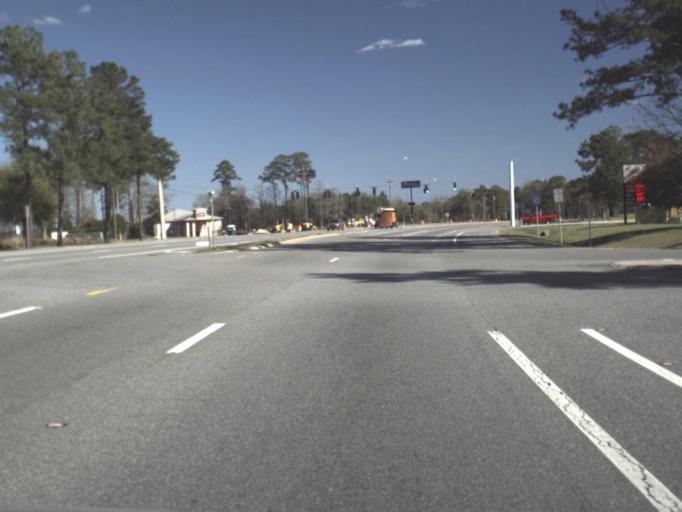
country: US
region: Florida
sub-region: Gadsden County
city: Midway
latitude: 30.4944
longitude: -84.4299
